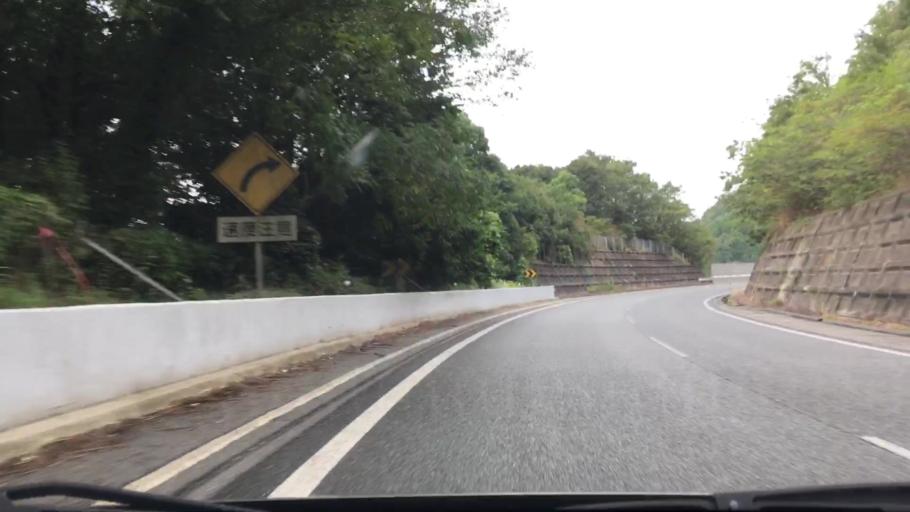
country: JP
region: Okayama
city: Niimi
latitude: 34.9898
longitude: 133.4616
